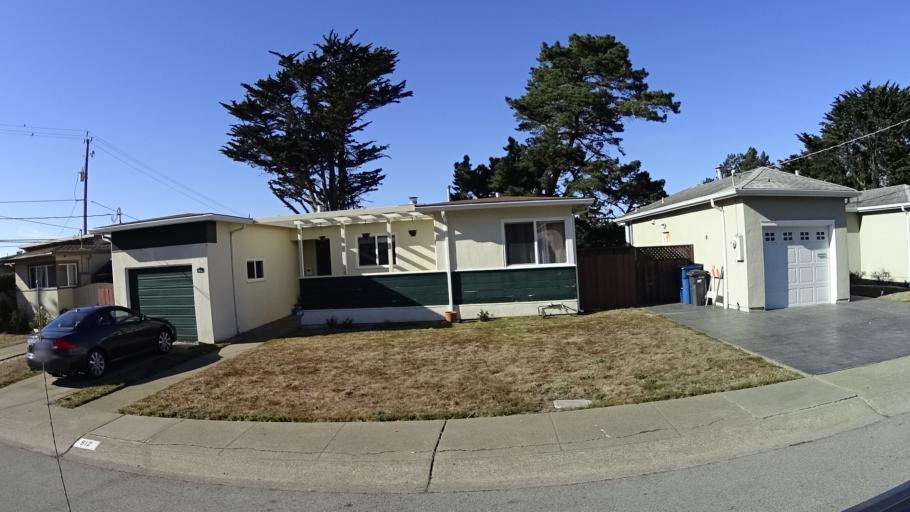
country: US
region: California
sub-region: San Mateo County
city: Broadmoor
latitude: 37.6930
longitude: -122.4885
